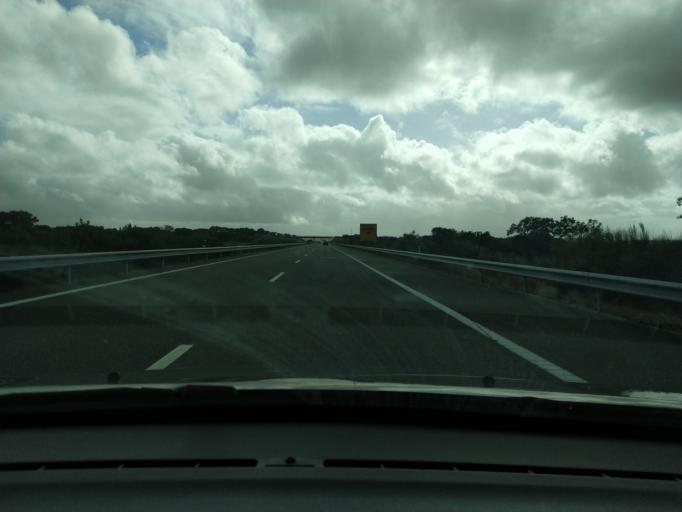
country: PT
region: Beja
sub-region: Ourique
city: Ourique
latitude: 37.5893
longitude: -8.1798
